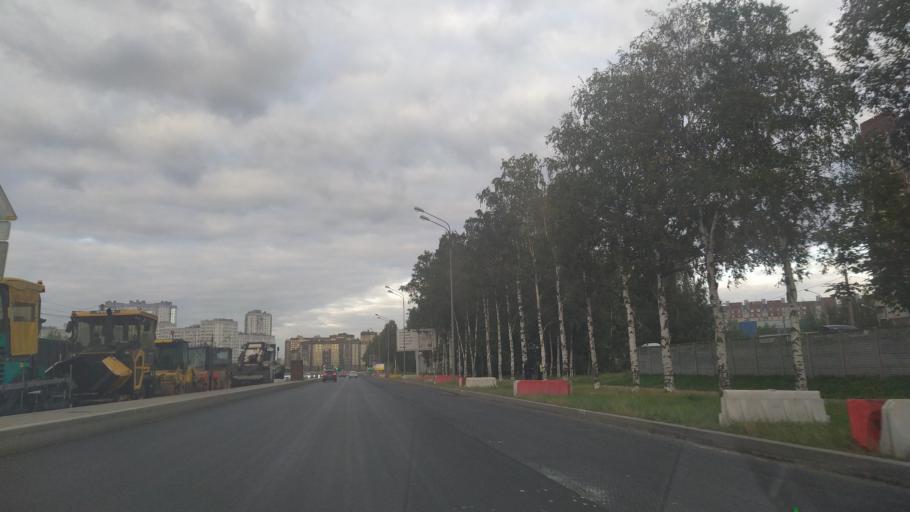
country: RU
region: Leningrad
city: Untolovo
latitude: 59.9933
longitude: 30.1992
